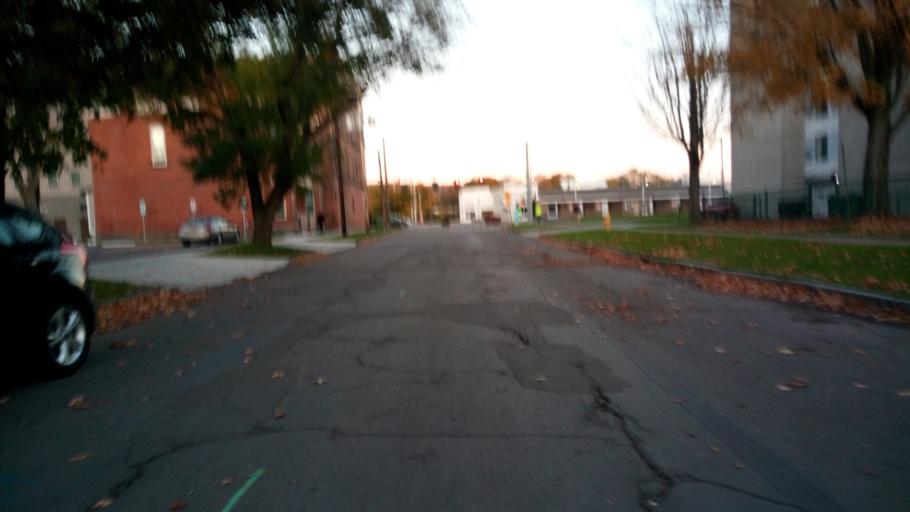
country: US
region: New York
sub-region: Chemung County
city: Elmira
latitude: 42.0822
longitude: -76.8060
